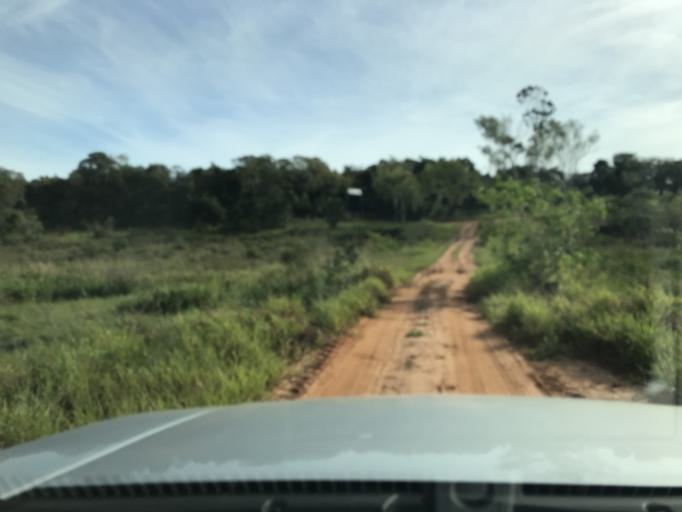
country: BR
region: Mato Grosso do Sul
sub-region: Iguatemi
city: Iguatemi
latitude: -23.6461
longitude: -54.5766
